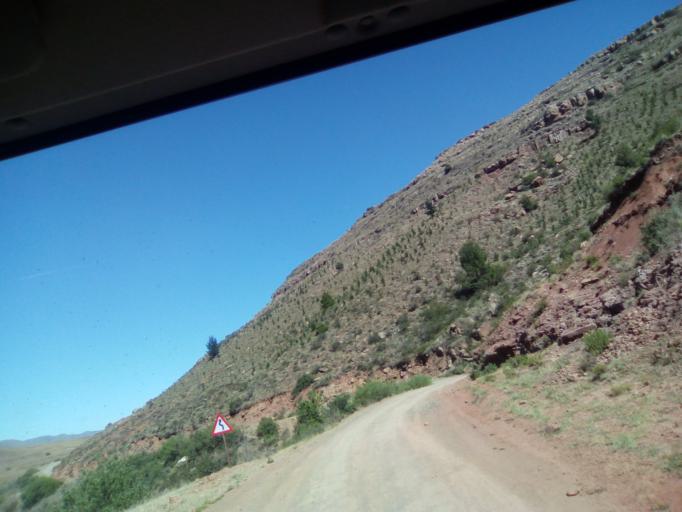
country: LS
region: Qacha's Nek
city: Qacha's Nek
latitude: -30.0575
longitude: 28.6406
